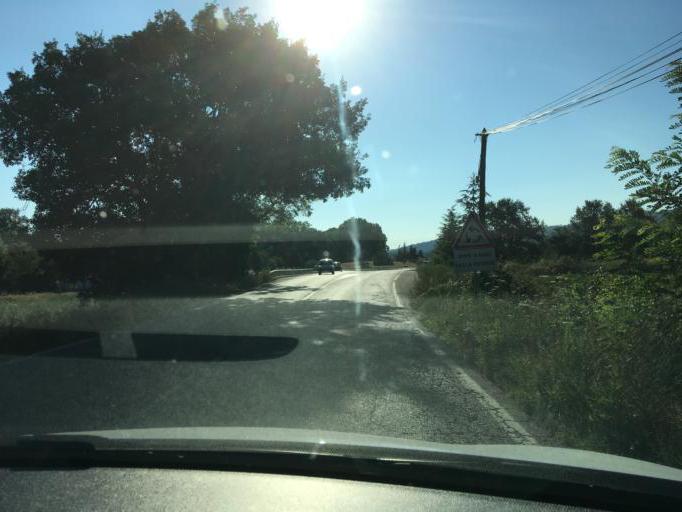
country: FR
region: Provence-Alpes-Cote d'Azur
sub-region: Departement des Bouches-du-Rhone
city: Charleval
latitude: 43.7167
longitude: 5.2222
